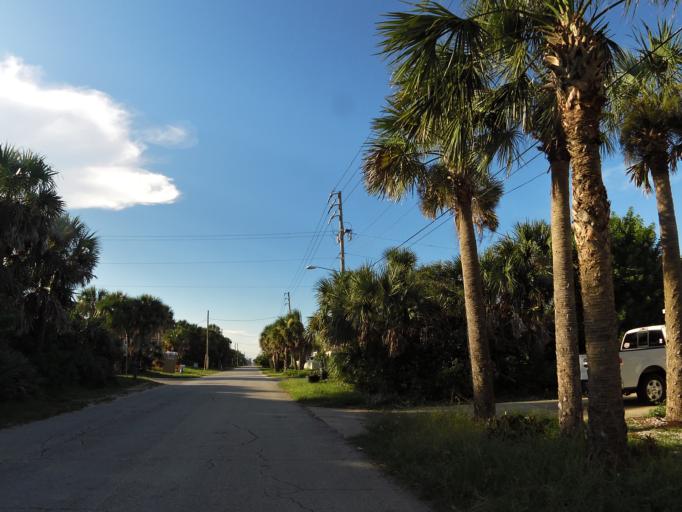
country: US
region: Florida
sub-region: Flagler County
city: Flagler Beach
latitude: 29.4666
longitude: -81.1217
